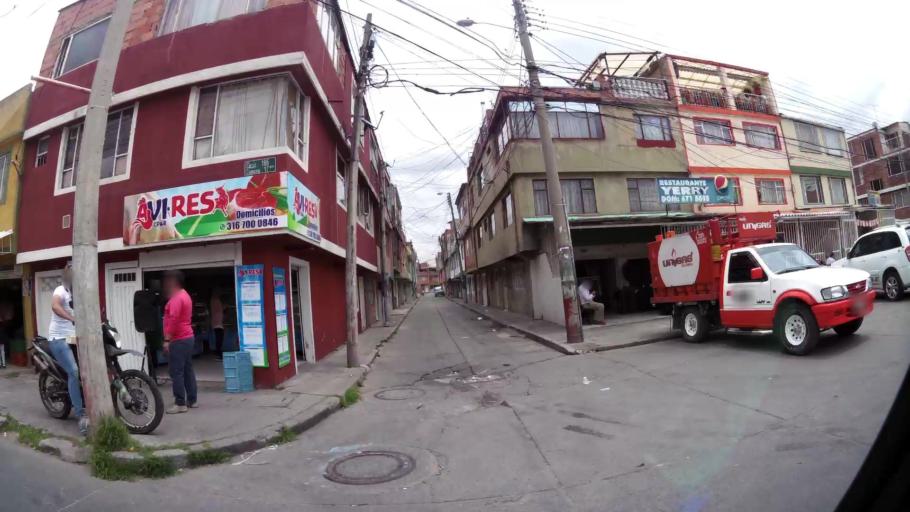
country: CO
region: Cundinamarca
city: Cota
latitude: 4.7629
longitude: -74.0386
